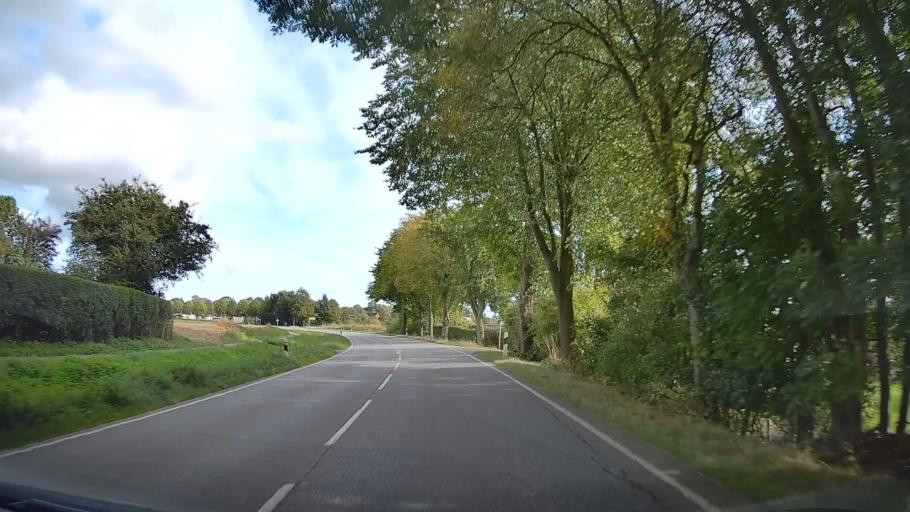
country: DE
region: Schleswig-Holstein
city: Stangheck
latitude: 54.7439
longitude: 9.8721
